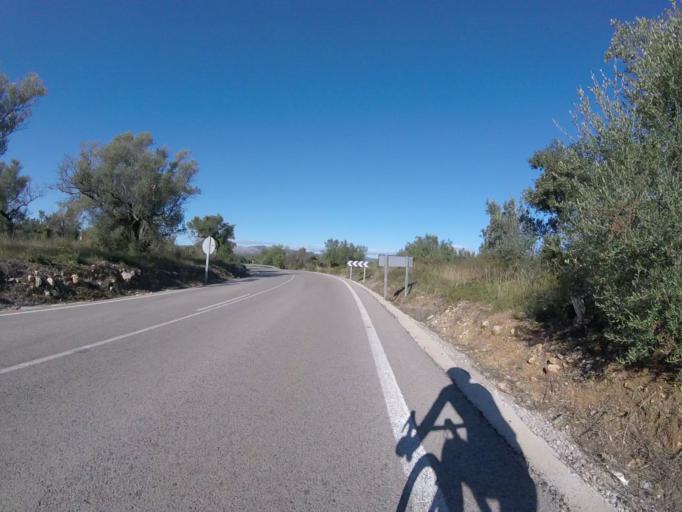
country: ES
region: Valencia
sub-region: Provincia de Castello
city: Cervera del Maestre
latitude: 40.4768
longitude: 0.2213
